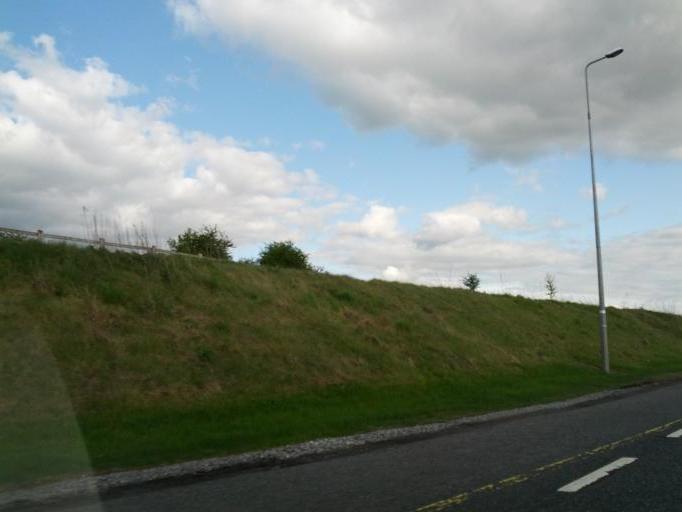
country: IE
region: Leinster
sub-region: An Iarmhi
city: Athlone
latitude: 53.4098
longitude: -7.8837
